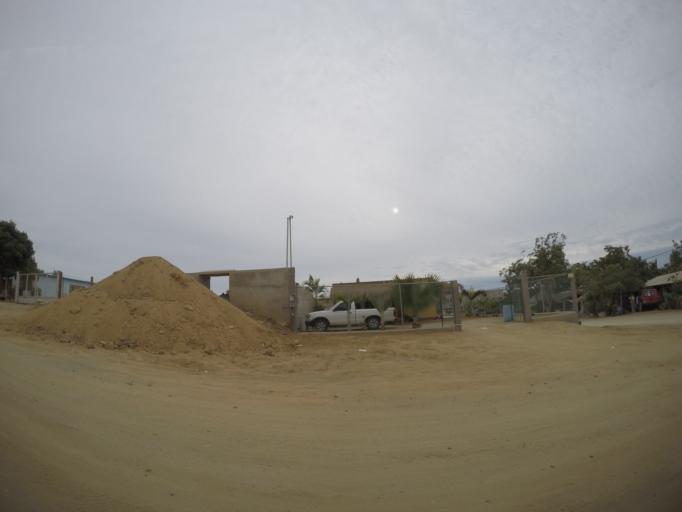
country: MX
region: Baja California Sur
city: Todos Santos
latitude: 23.4432
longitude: -110.2243
